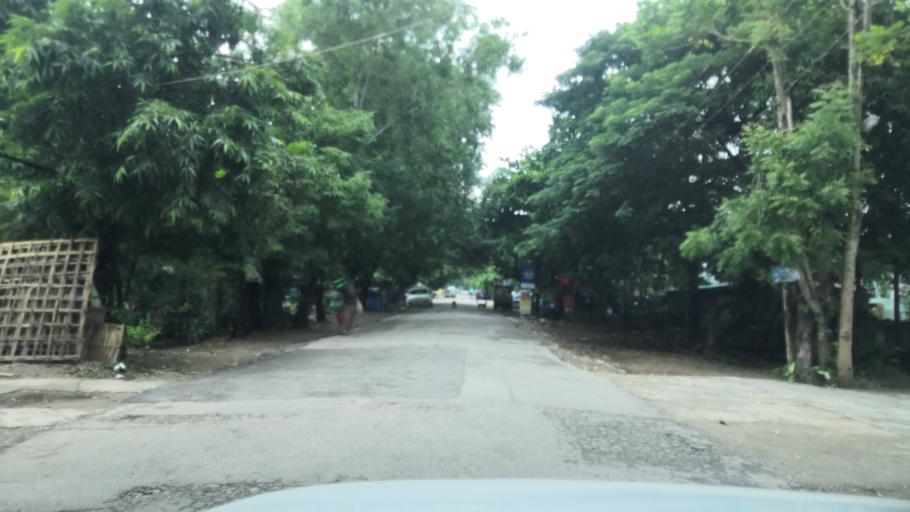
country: MM
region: Yangon
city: Yangon
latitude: 16.8874
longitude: 96.1760
